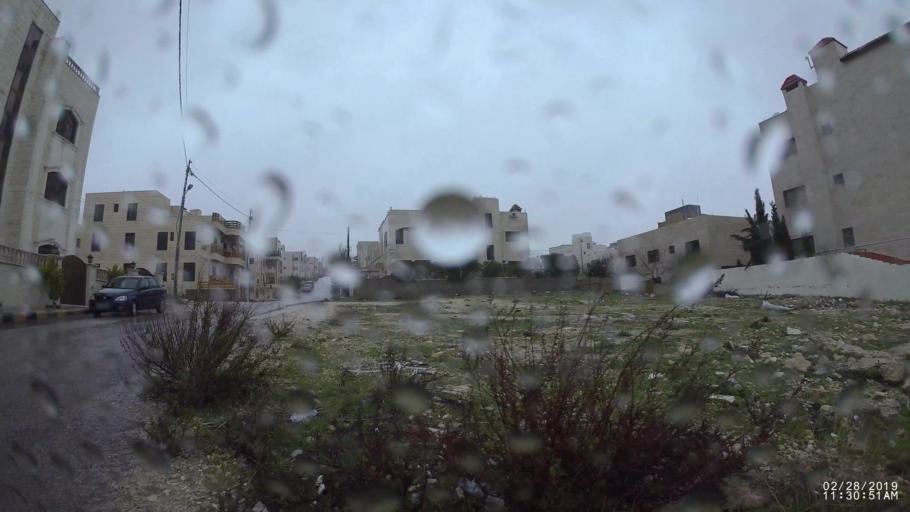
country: JO
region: Amman
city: Al Jubayhah
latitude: 32.0077
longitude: 35.8985
